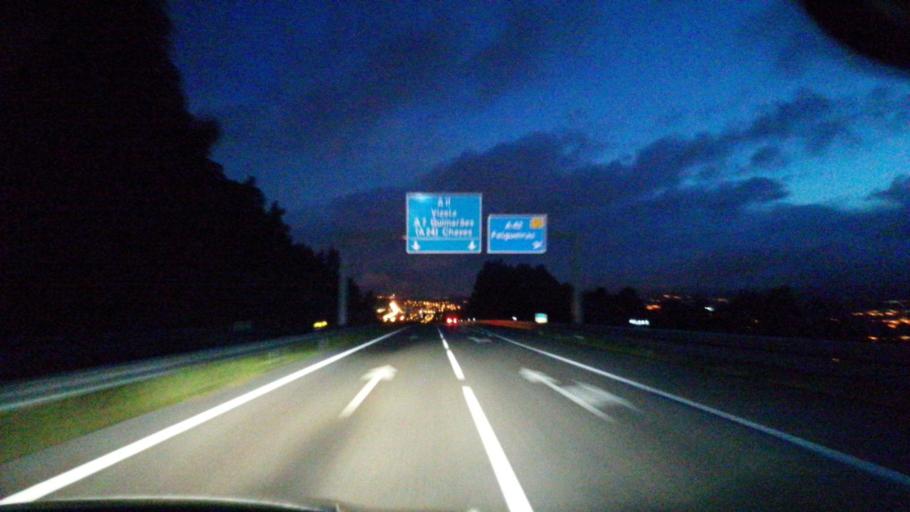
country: PT
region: Porto
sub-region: Lousada
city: Lousada
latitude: 41.3209
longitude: -8.2405
